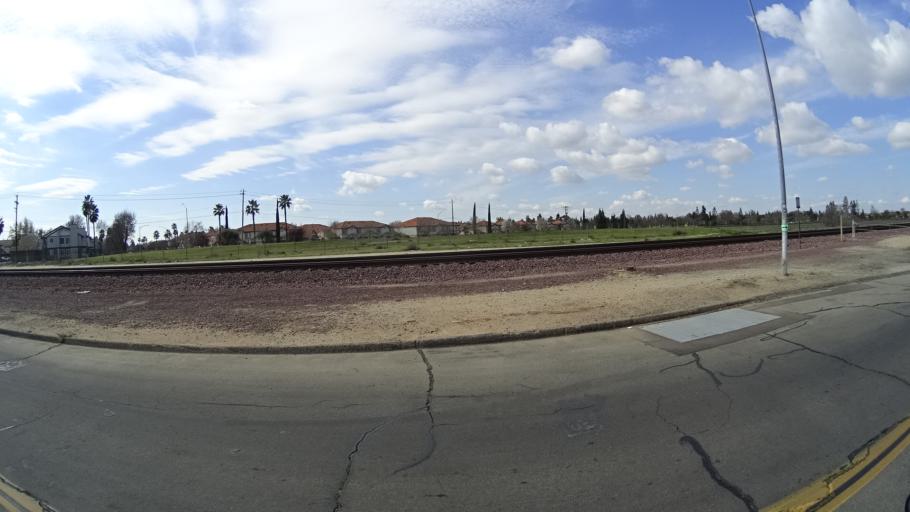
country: US
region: California
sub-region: Fresno County
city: Fresno
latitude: 36.8164
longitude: -119.8533
